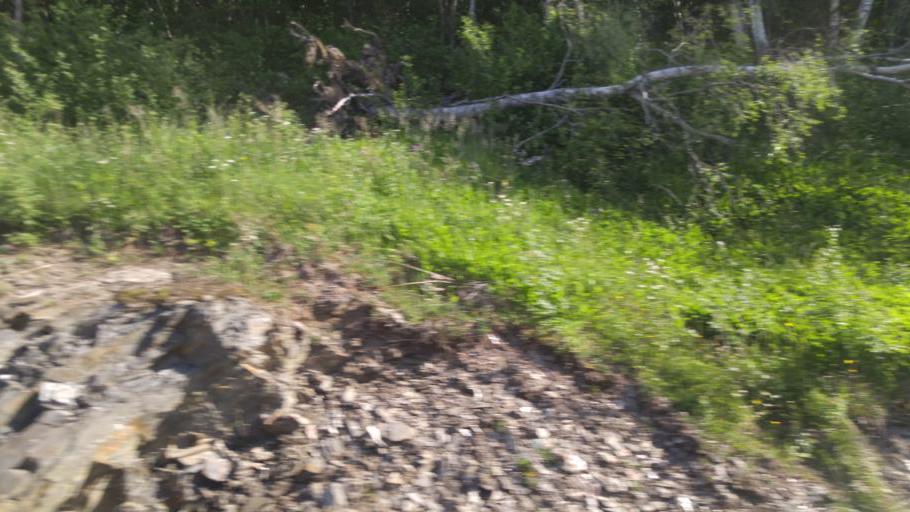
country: NO
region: Nord-Trondelag
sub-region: Meraker
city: Meraker
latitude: 63.4024
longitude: 11.7844
